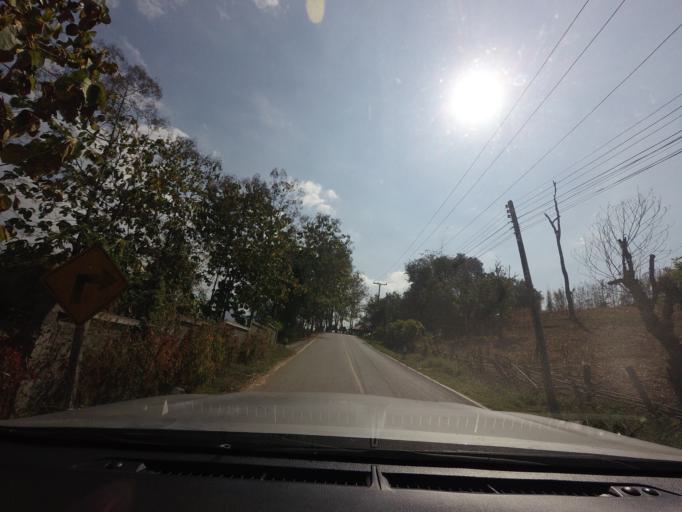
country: TH
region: Mae Hong Son
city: Wiang Nuea
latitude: 19.4002
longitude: 98.4426
